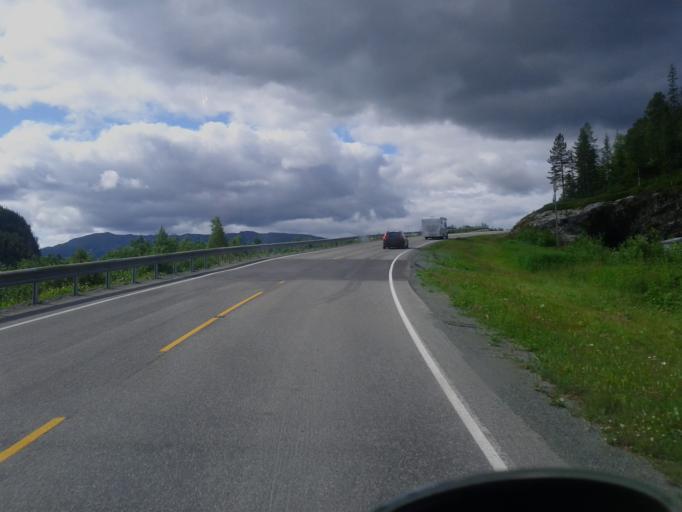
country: NO
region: Nord-Trondelag
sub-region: Grong
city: Grong
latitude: 64.5370
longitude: 12.4446
